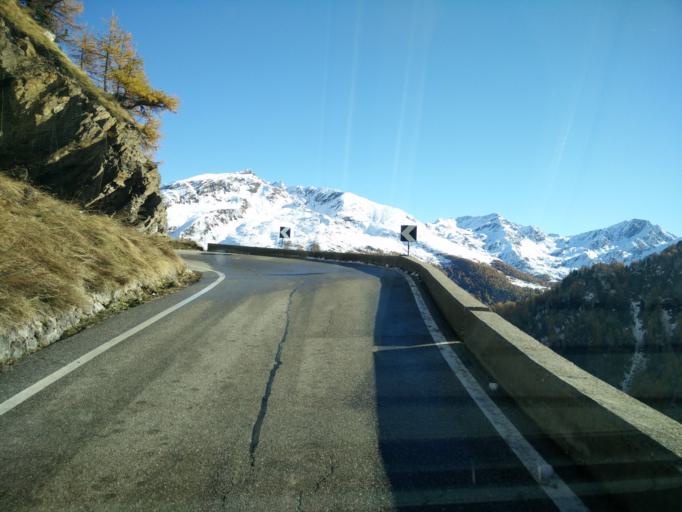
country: IT
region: Trentino-Alto Adige
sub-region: Bolzano
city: Moso in Passiria
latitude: 46.8820
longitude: 11.1152
